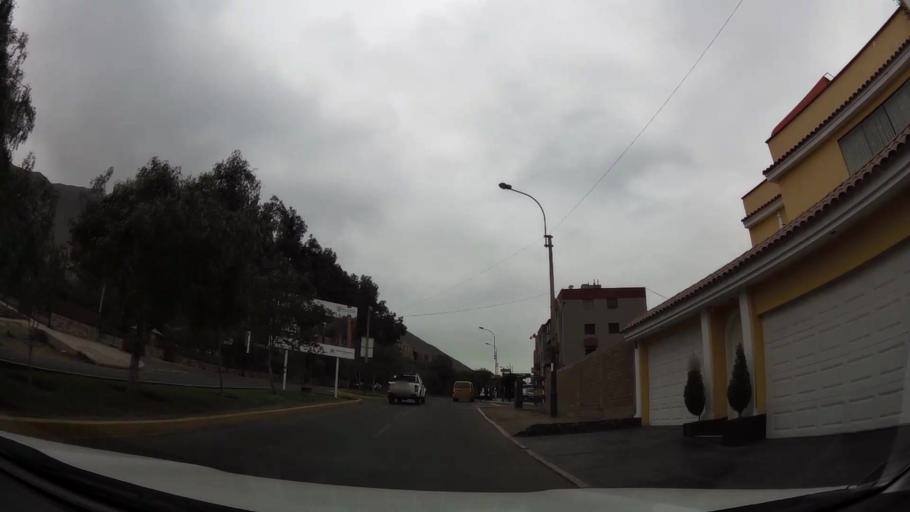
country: PE
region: Lima
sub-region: Lima
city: La Molina
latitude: -12.1057
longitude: -76.9574
